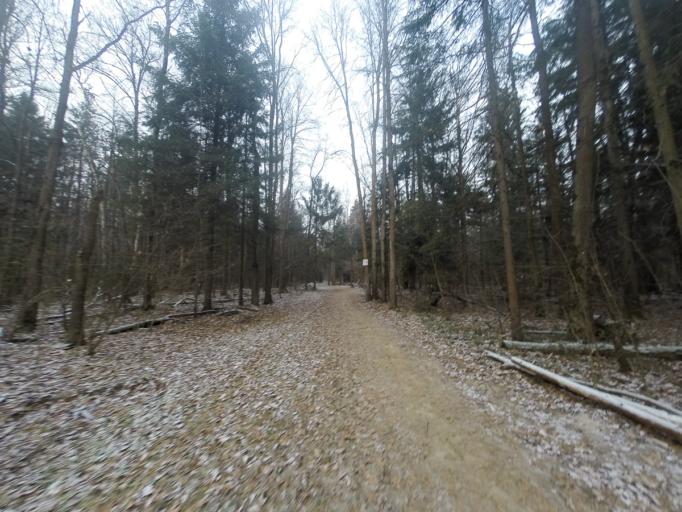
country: RU
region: Moskovskaya
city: Krasnogorsk
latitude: 55.8487
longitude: 37.3007
